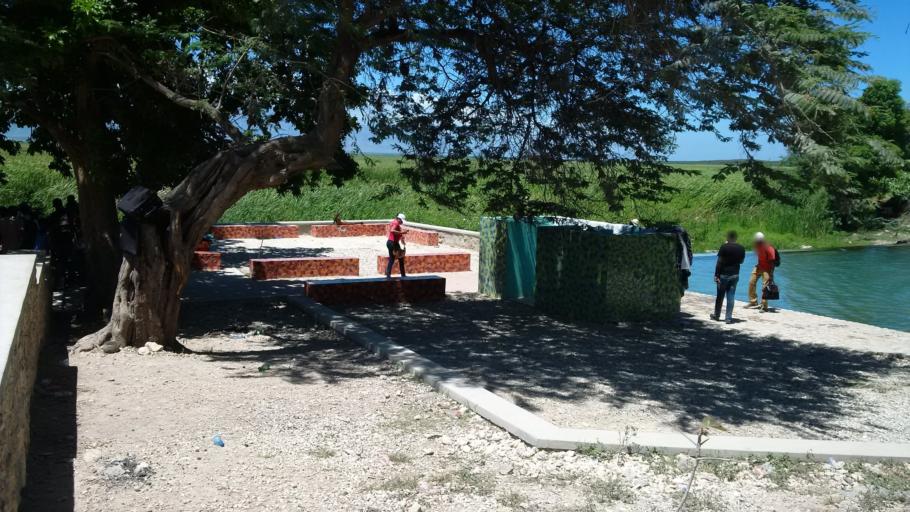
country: HT
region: Ouest
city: Thomazeau
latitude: 18.6570
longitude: -72.1330
